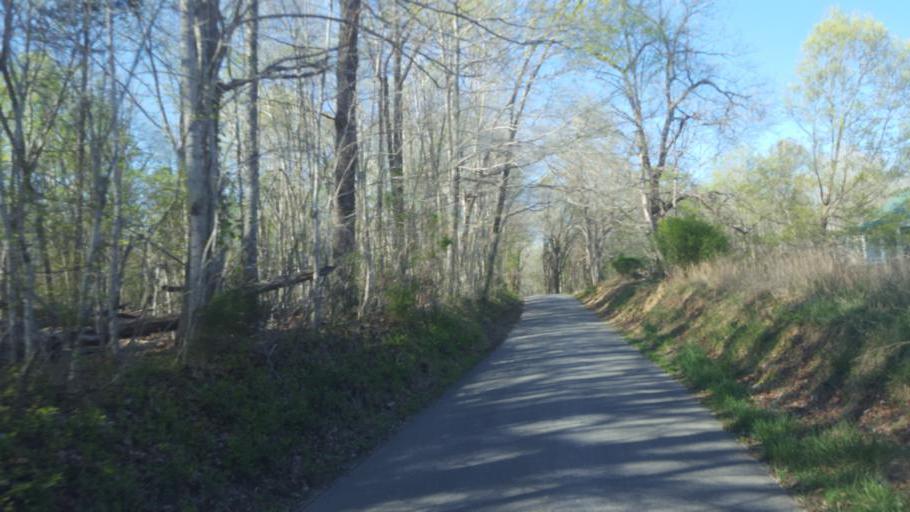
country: US
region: Kentucky
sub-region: Barren County
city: Cave City
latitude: 37.1830
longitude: -86.0493
